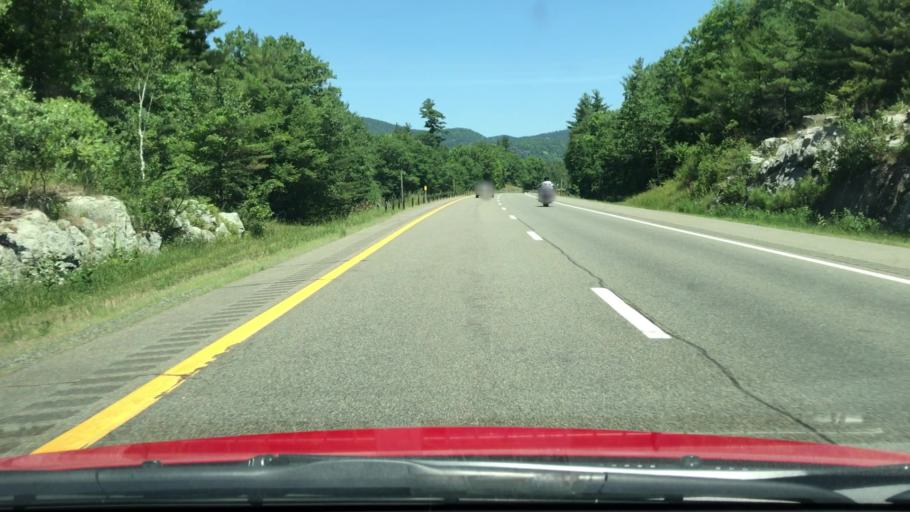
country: US
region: New York
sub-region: Essex County
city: Elizabethtown
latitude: 44.3517
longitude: -73.5332
